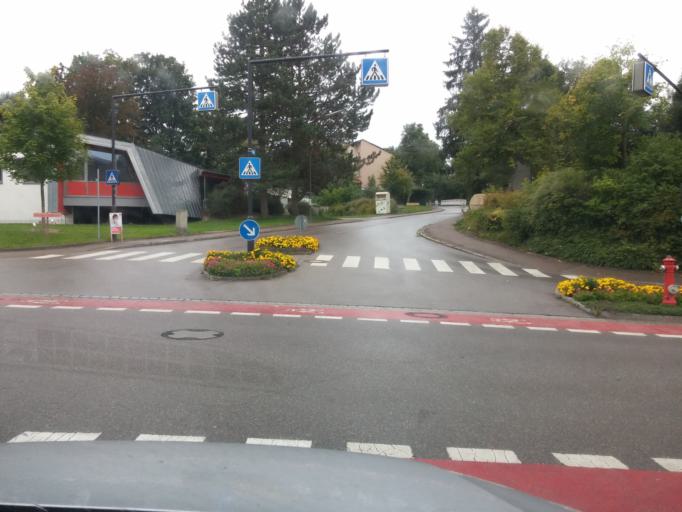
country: DE
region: Bavaria
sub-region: Upper Bavaria
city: Pfaffenhofen an der Ilm
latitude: 48.5270
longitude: 11.5135
